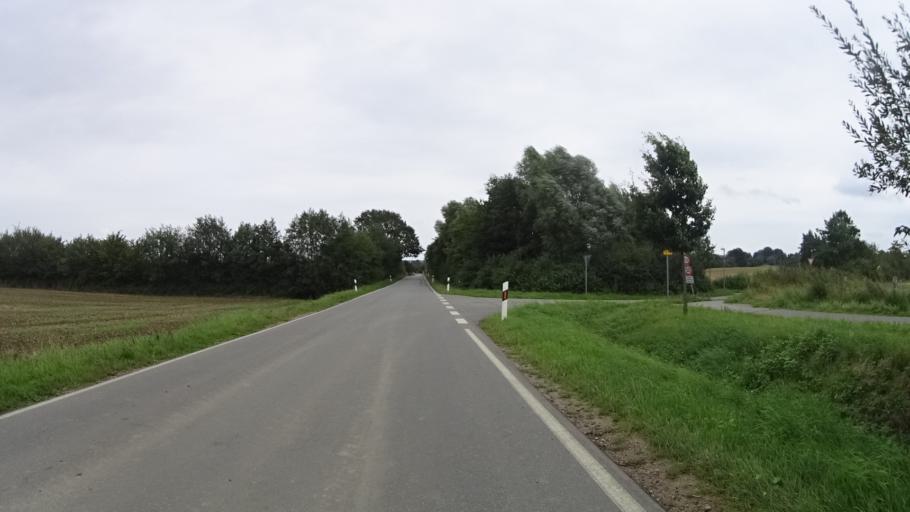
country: DE
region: Schleswig-Holstein
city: Labenz
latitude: 53.7138
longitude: 10.5073
